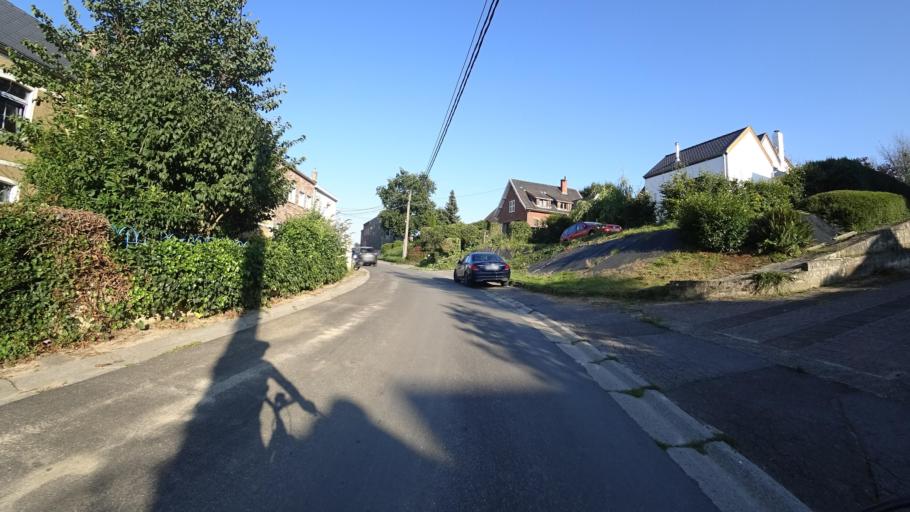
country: BE
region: Wallonia
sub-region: Province du Brabant Wallon
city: Mont-Saint-Guibert
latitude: 50.6314
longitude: 4.6194
